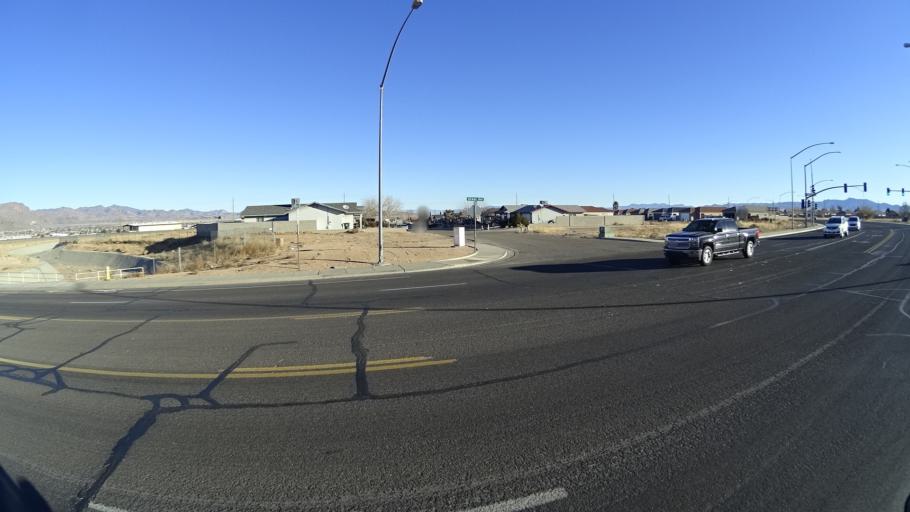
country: US
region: Arizona
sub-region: Mohave County
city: New Kingman-Butler
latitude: 35.2223
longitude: -113.9996
